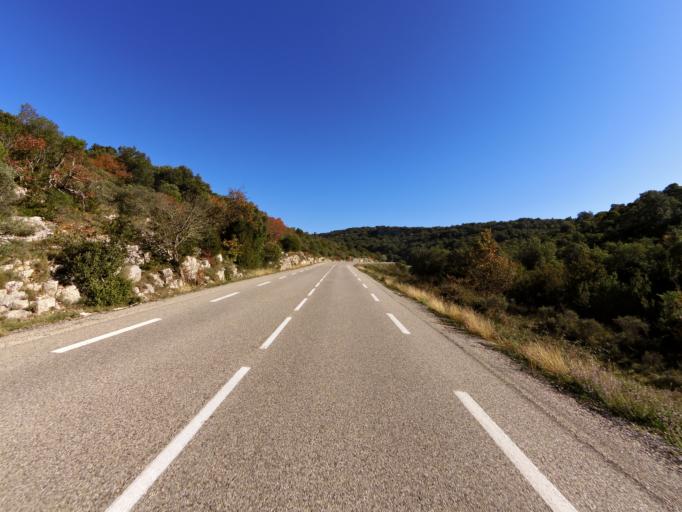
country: FR
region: Rhone-Alpes
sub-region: Departement de l'Ardeche
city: Ruoms
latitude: 44.4058
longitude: 4.4490
